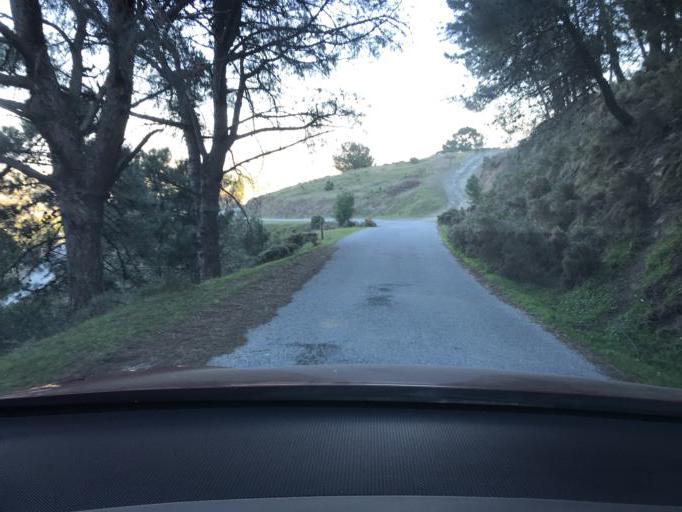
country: ES
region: Andalusia
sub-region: Provincia de Malaga
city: Tolox
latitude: 36.6814
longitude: -4.9153
